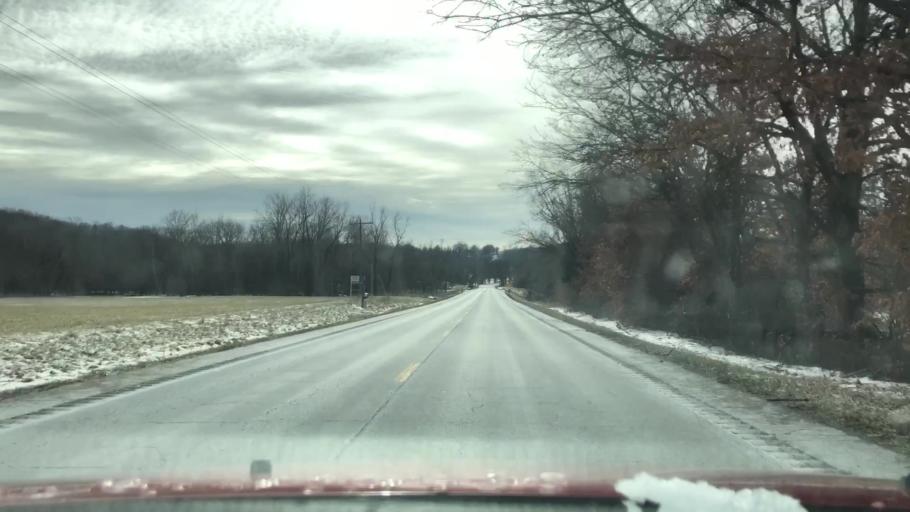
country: US
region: Missouri
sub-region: Jackson County
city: Oak Grove
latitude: 38.9459
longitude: -94.1319
